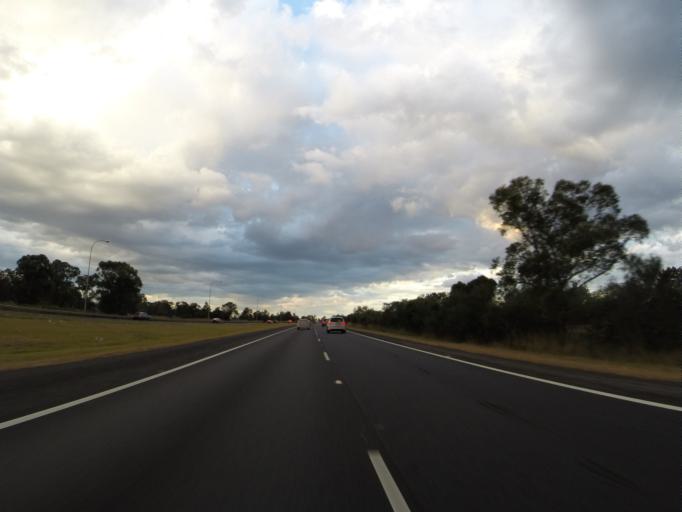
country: AU
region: New South Wales
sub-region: Wollondilly
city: Douglas Park
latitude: -34.2277
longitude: 150.6691
